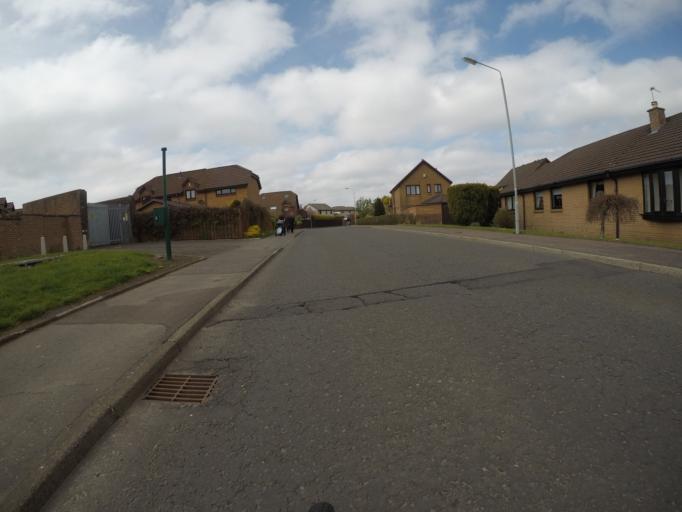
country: GB
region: Scotland
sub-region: East Renfrewshire
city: Newton Mearns
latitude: 55.7780
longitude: -4.3484
